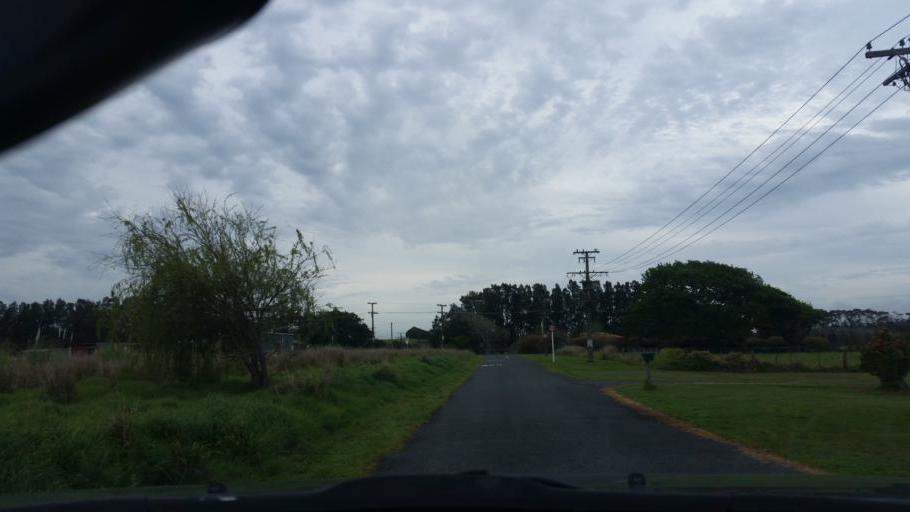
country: NZ
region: Northland
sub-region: Kaipara District
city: Dargaville
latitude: -35.9358
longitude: 173.8514
